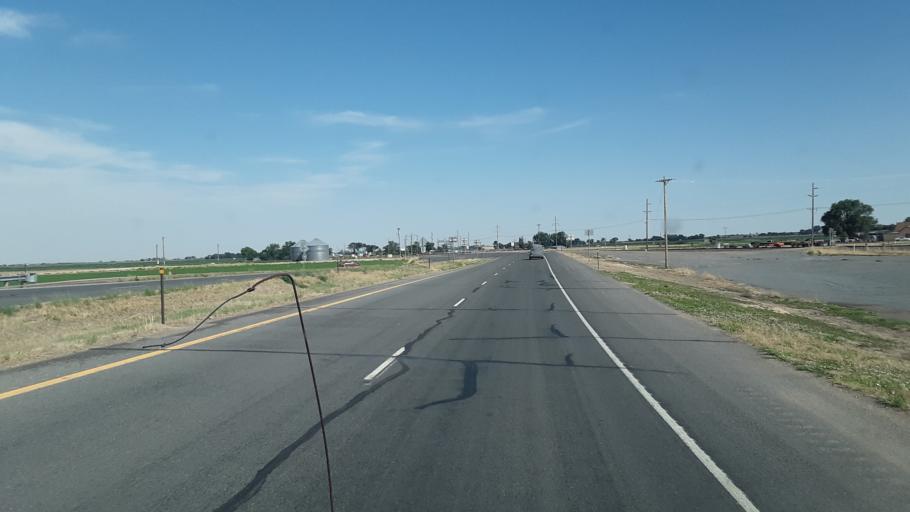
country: US
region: Colorado
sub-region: Otero County
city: Rocky Ford
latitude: 38.1021
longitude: -103.8395
